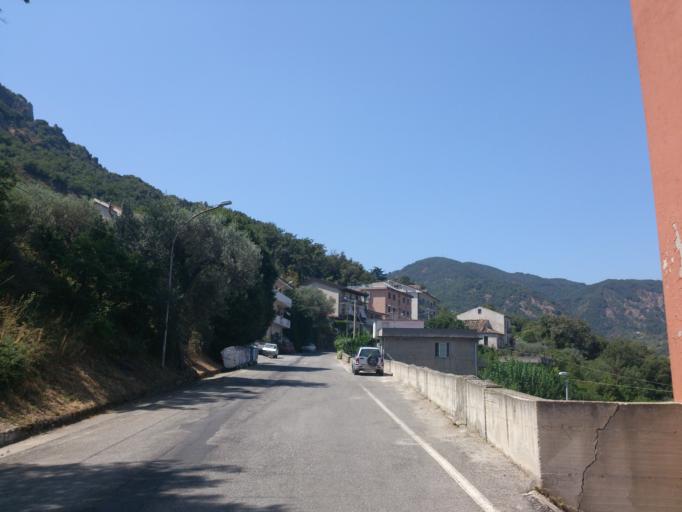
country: IT
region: Calabria
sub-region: Provincia di Reggio Calabria
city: Pazzano
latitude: 38.4773
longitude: 16.4497
